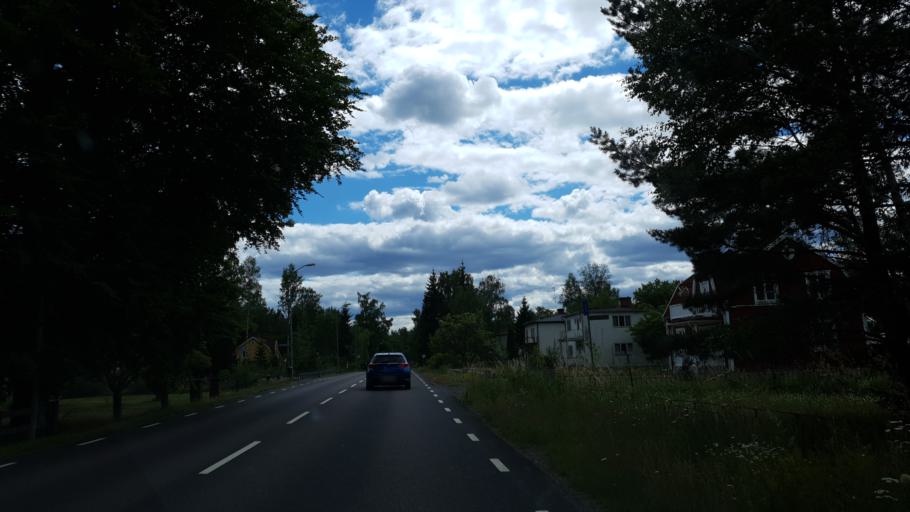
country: SE
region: Kalmar
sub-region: Emmaboda Kommun
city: Emmaboda
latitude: 56.9202
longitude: 15.5715
